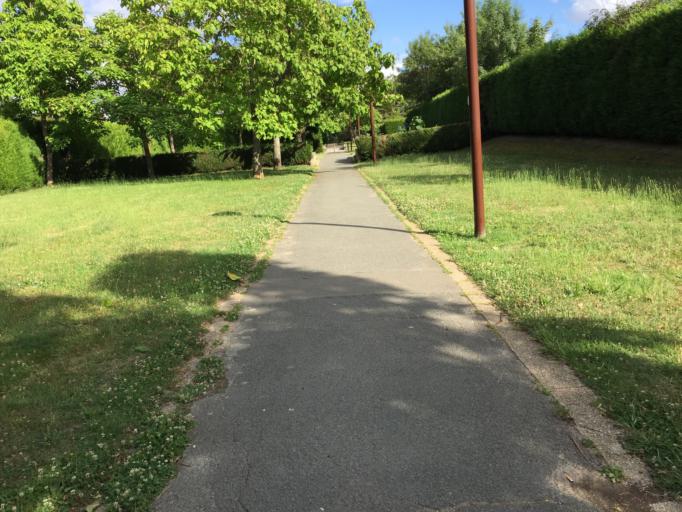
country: FR
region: Ile-de-France
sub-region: Departement des Yvelines
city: Guyancourt
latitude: 48.7734
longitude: 2.0655
